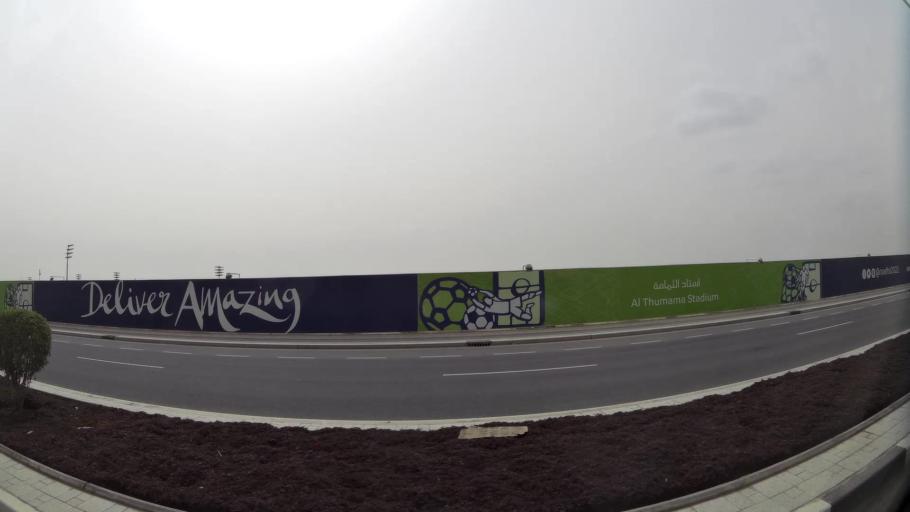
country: QA
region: Baladiyat ad Dawhah
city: Doha
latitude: 25.2337
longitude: 51.5346
